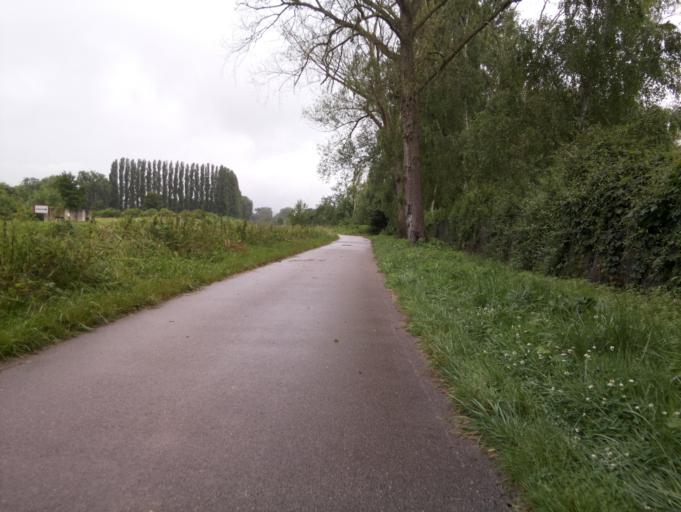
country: FR
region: Picardie
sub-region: Departement de la Somme
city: Ailly-sur-Somme
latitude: 49.9287
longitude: 2.2043
